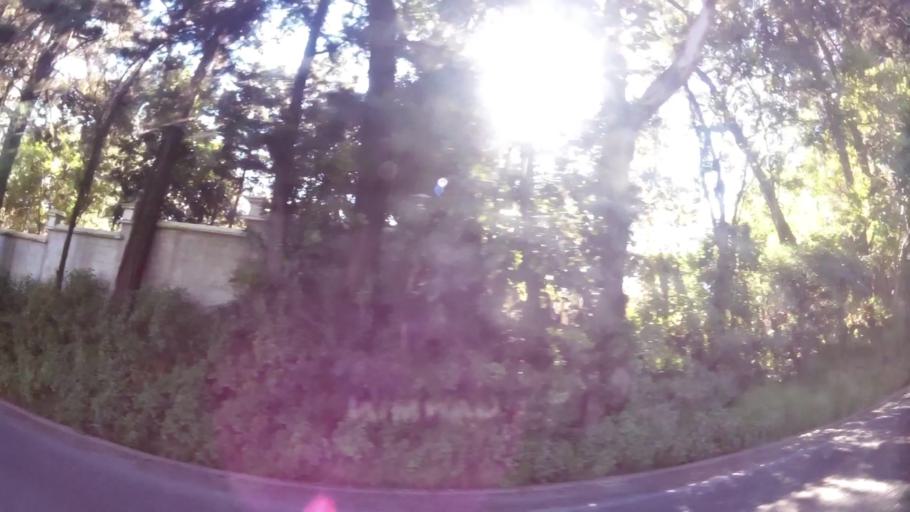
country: GT
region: Sacatepequez
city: Santa Lucia Milpas Altas
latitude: 14.5782
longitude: -90.6489
